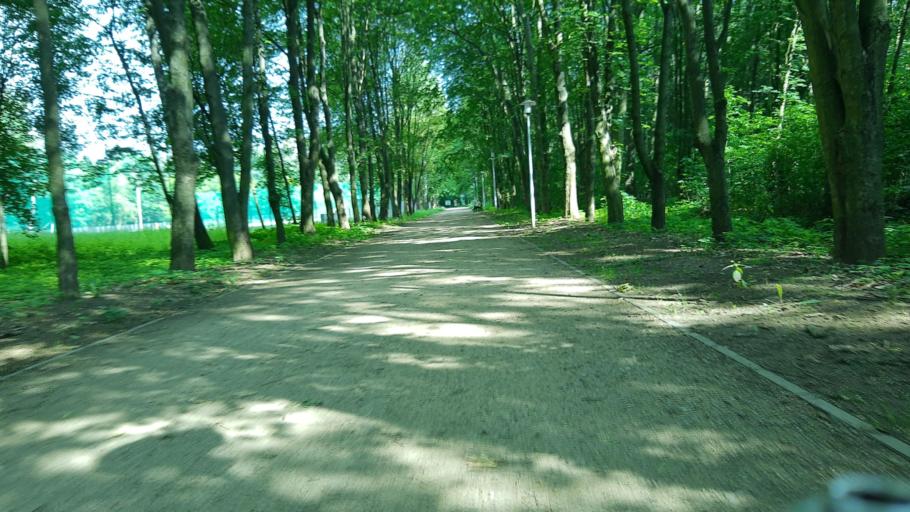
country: PL
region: Lodz Voivodeship
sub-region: Powiat sieradzki
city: Sieradz
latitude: 51.5964
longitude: 18.7535
